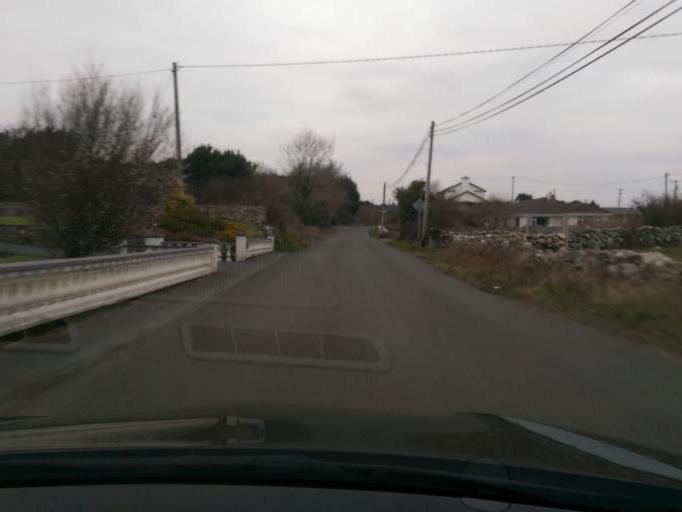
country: IE
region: Connaught
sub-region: County Galway
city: Bearna
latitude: 53.2538
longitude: -9.1533
